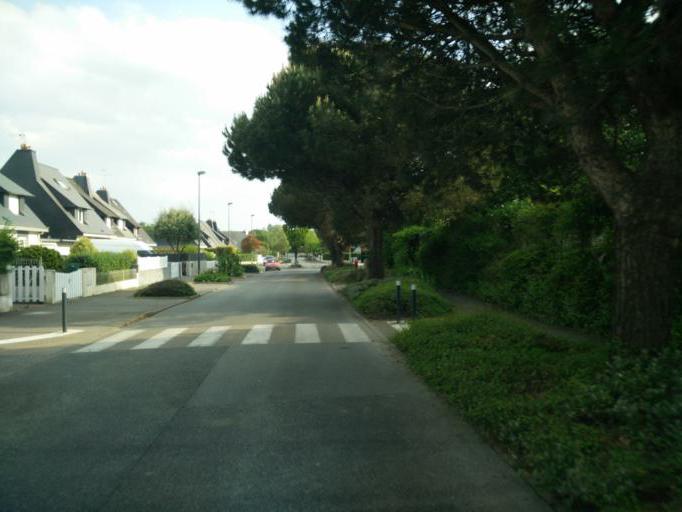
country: FR
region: Brittany
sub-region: Departement du Morbihan
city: Ploemeur
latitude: 47.7346
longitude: -3.4328
